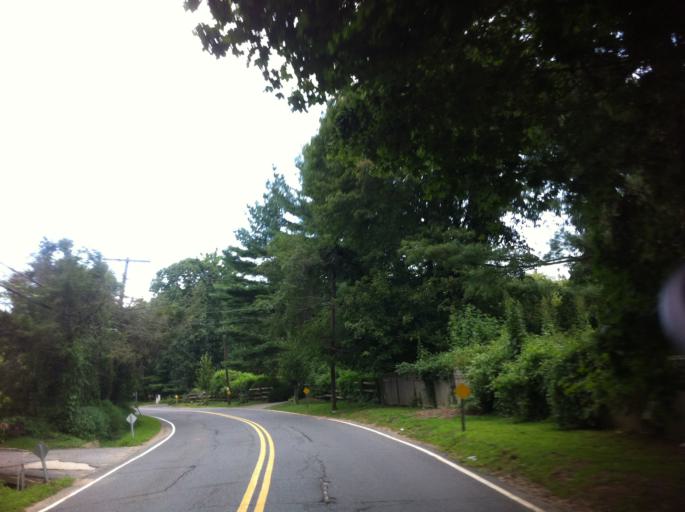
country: US
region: New York
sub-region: Nassau County
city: Old Brookville
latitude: 40.8322
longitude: -73.6053
